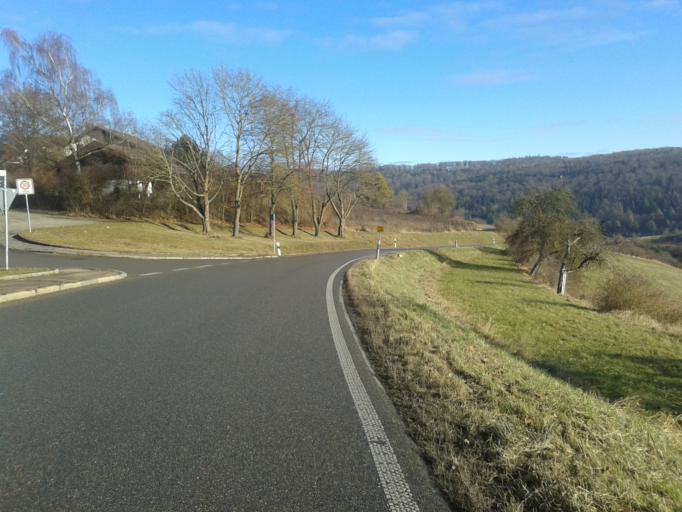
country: DE
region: Baden-Wuerttemberg
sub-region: Tuebingen Region
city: Erbach
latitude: 48.3981
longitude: 9.8651
